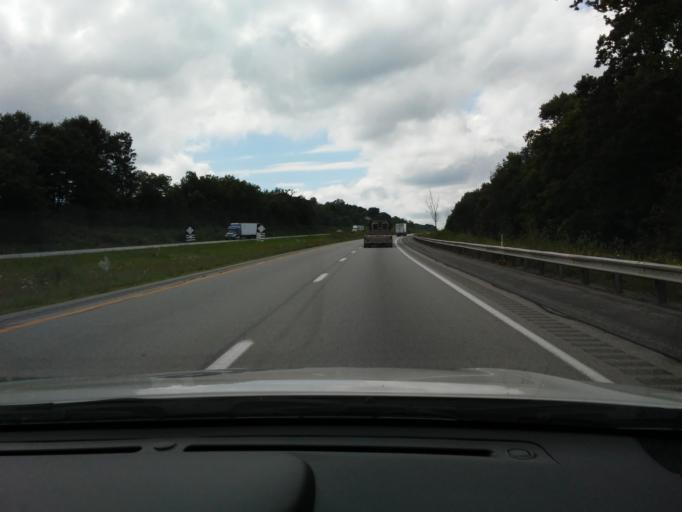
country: US
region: Pennsylvania
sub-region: Mercer County
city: Grove City
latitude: 41.1971
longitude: -79.8915
